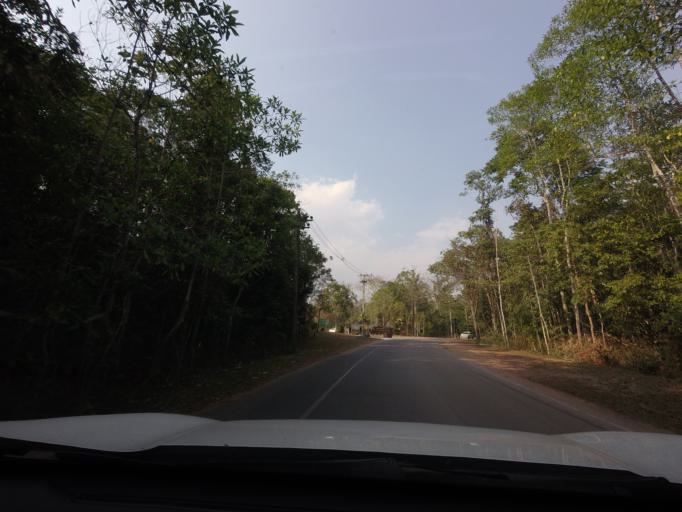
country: TH
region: Nakhon Nayok
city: Nakhon Nayok
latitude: 14.4223
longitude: 101.3884
